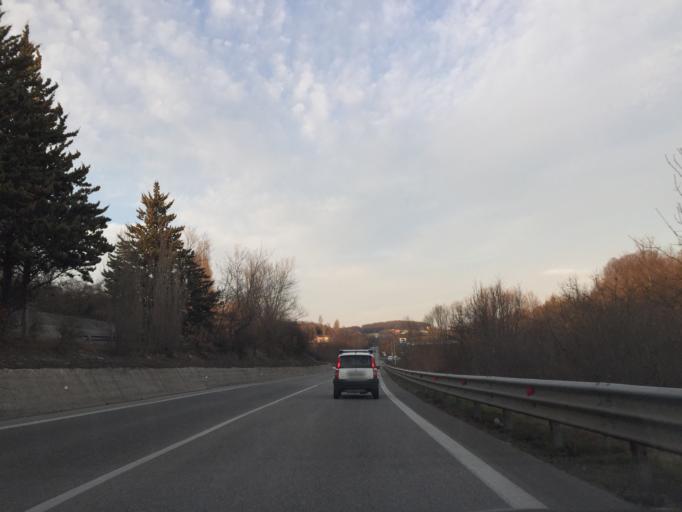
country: IT
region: Molise
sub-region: Provincia di Campobasso
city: Vinchiaturo
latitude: 41.5370
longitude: 14.6158
